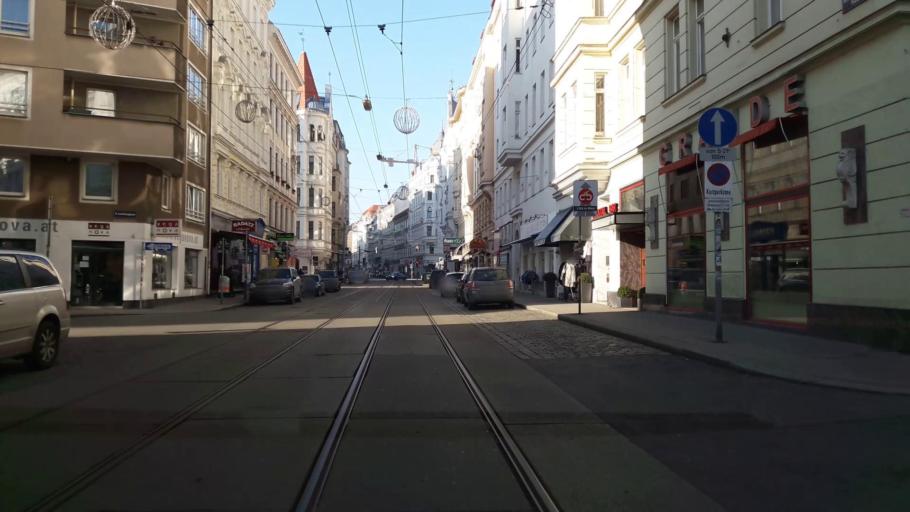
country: AT
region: Vienna
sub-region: Wien Stadt
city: Vienna
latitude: 48.2102
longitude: 16.3458
